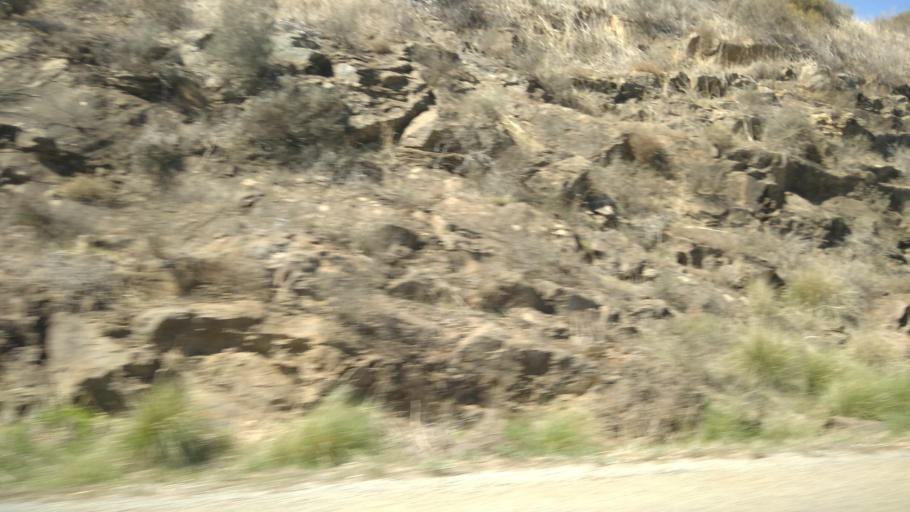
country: ZA
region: Western Cape
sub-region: West Coast District Municipality
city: Malmesbury
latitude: -33.3803
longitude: 18.6680
